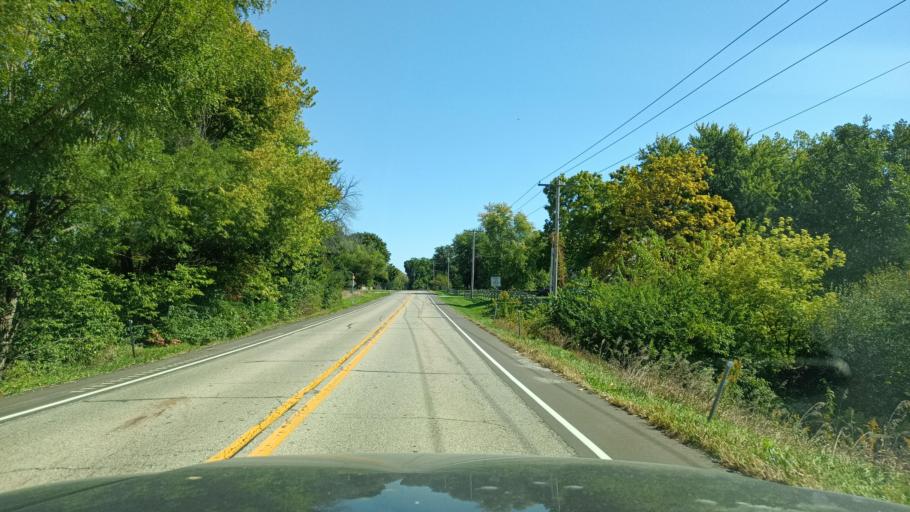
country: US
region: Illinois
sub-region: Woodford County
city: Eureka
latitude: 40.6273
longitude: -89.2591
